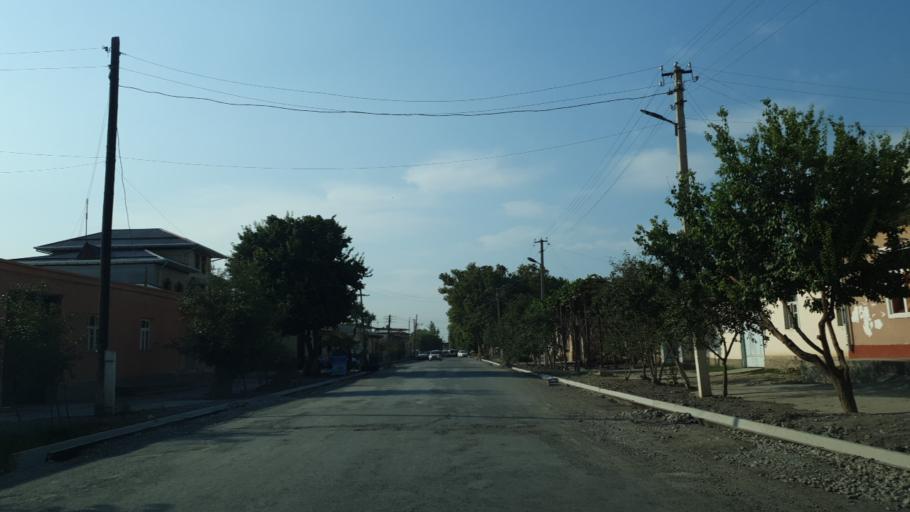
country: UZ
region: Fergana
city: Yaypan
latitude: 40.3771
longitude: 70.8116
